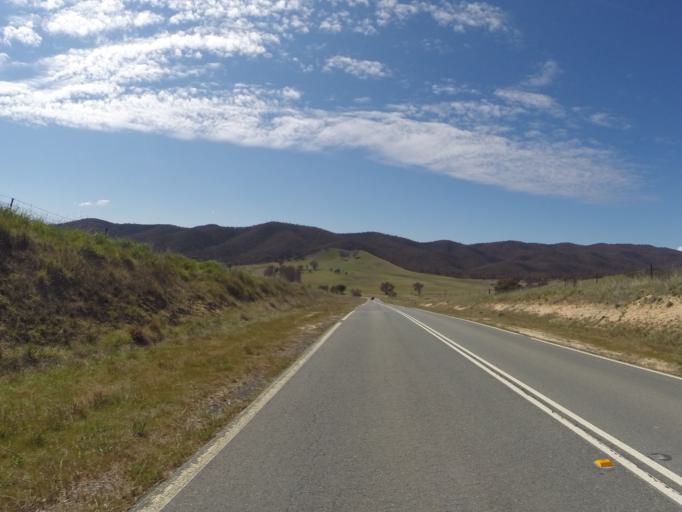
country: AU
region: Australian Capital Territory
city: Macarthur
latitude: -35.4117
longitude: 148.9764
